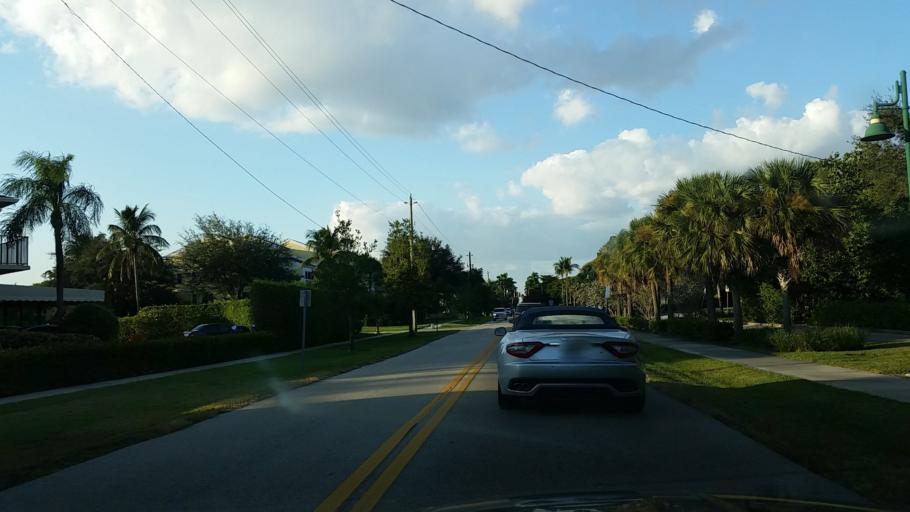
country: US
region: Florida
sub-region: Collier County
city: Naples
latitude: 26.1347
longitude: -81.7937
